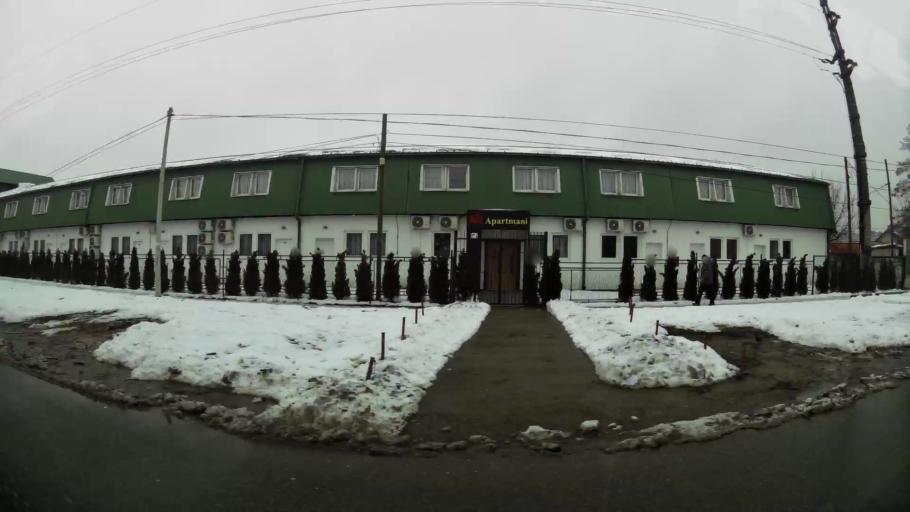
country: RS
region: Central Serbia
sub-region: Belgrade
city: Zemun
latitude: 44.8445
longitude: 20.3766
